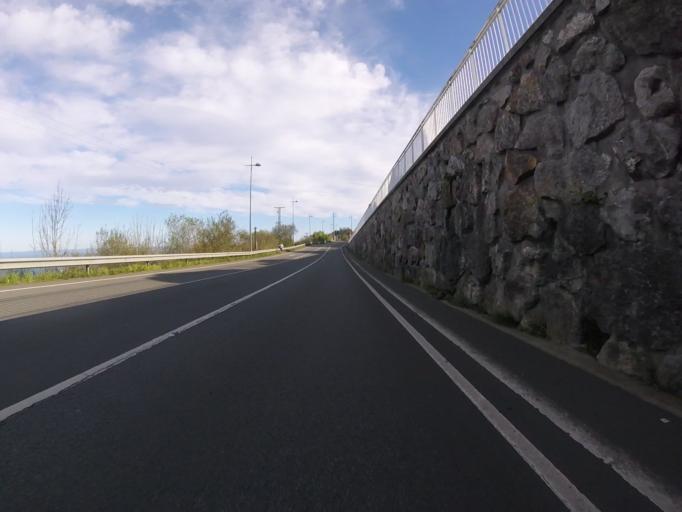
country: ES
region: Basque Country
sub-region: Provincia de Guipuzcoa
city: Usurbil
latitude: 43.3093
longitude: -2.0365
